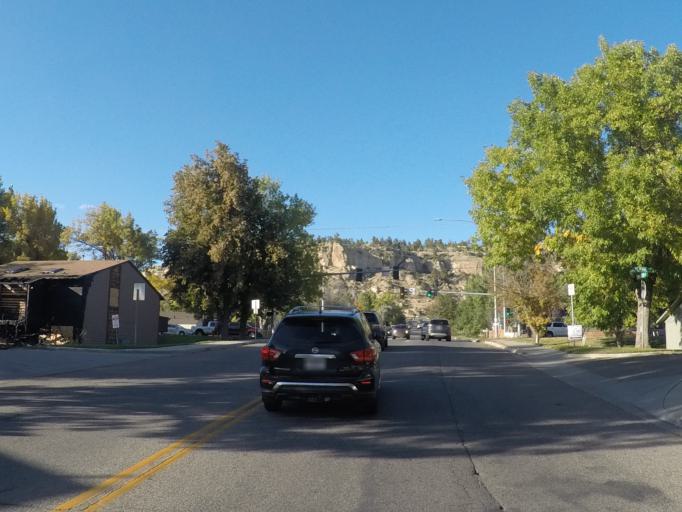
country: US
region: Montana
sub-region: Yellowstone County
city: Billings
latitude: 45.7980
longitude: -108.6019
